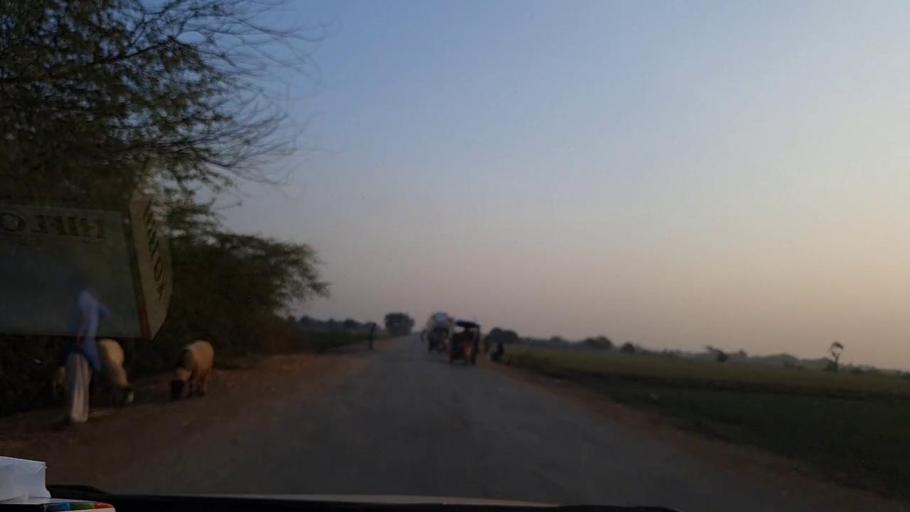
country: PK
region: Sindh
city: Tando Ghulam Ali
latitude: 25.1780
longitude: 68.9490
